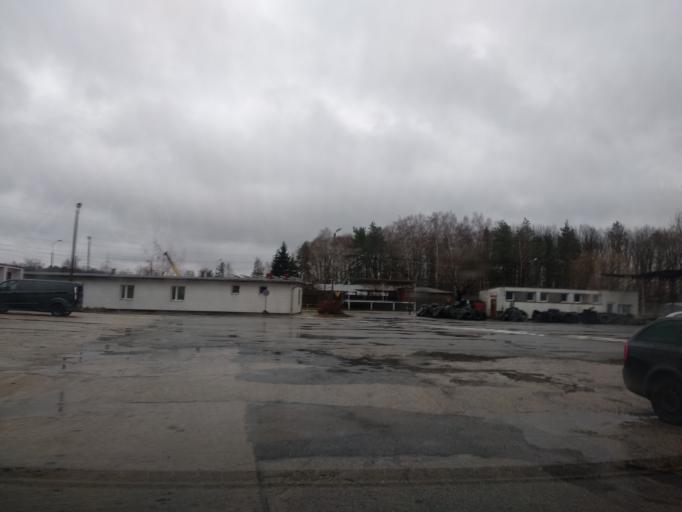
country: PL
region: Lower Silesian Voivodeship
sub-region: Powiat polkowicki
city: Polkowice
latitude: 51.5069
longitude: 16.0832
